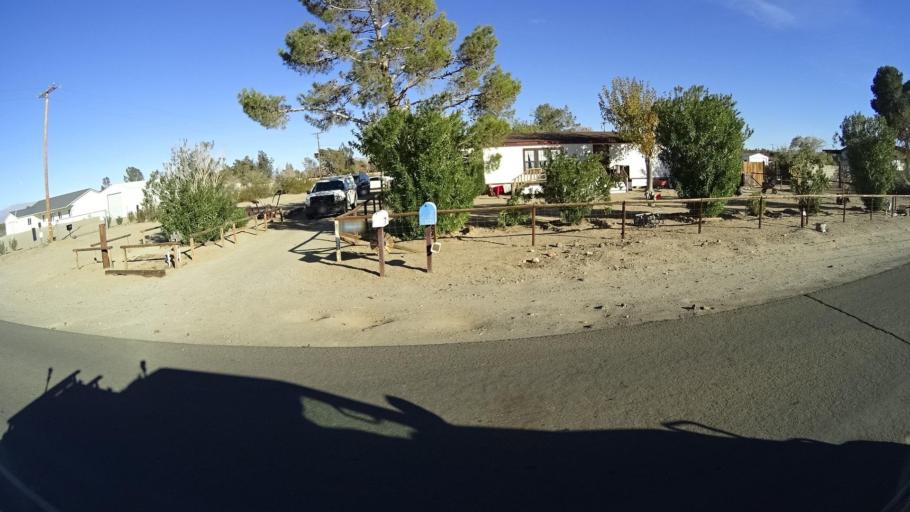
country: US
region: California
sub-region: Kern County
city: Ridgecrest
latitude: 35.6460
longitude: -117.7058
